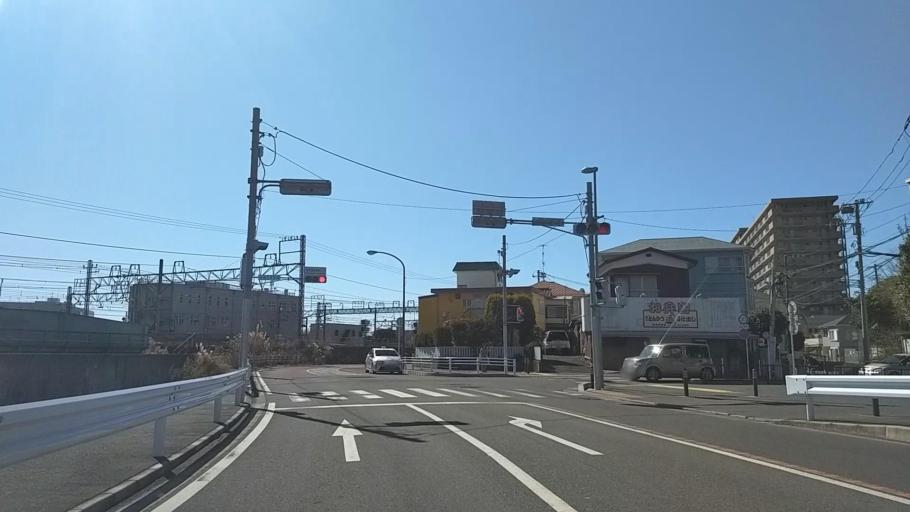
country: JP
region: Kanagawa
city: Kamakura
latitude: 35.3452
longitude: 139.5192
